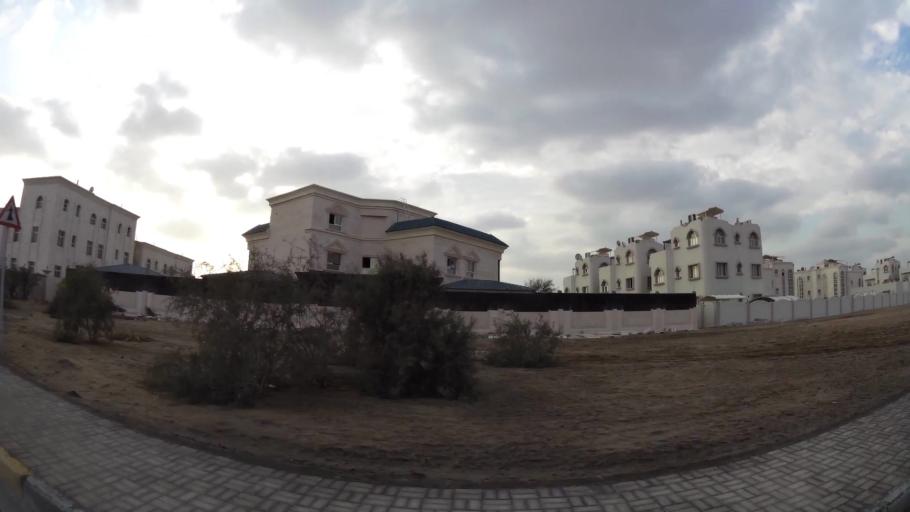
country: AE
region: Abu Dhabi
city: Abu Dhabi
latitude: 24.3569
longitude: 54.5585
